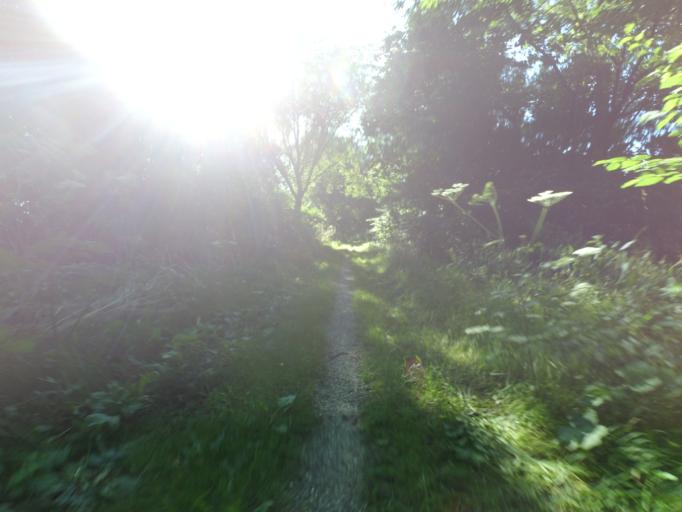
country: NL
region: Flevoland
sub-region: Gemeente Zeewolde
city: Zeewolde
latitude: 52.3963
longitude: 5.4927
